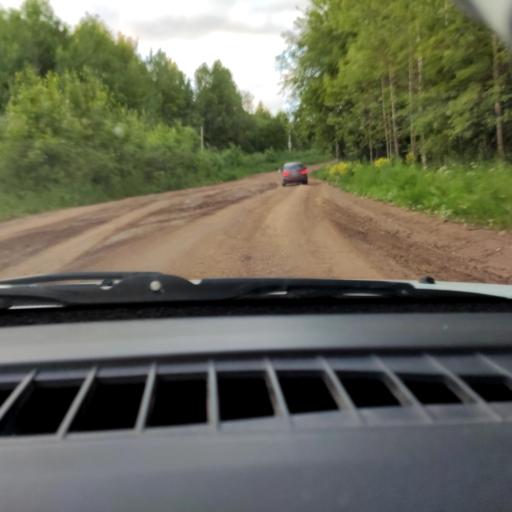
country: RU
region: Perm
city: Polazna
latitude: 58.1998
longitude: 56.4742
